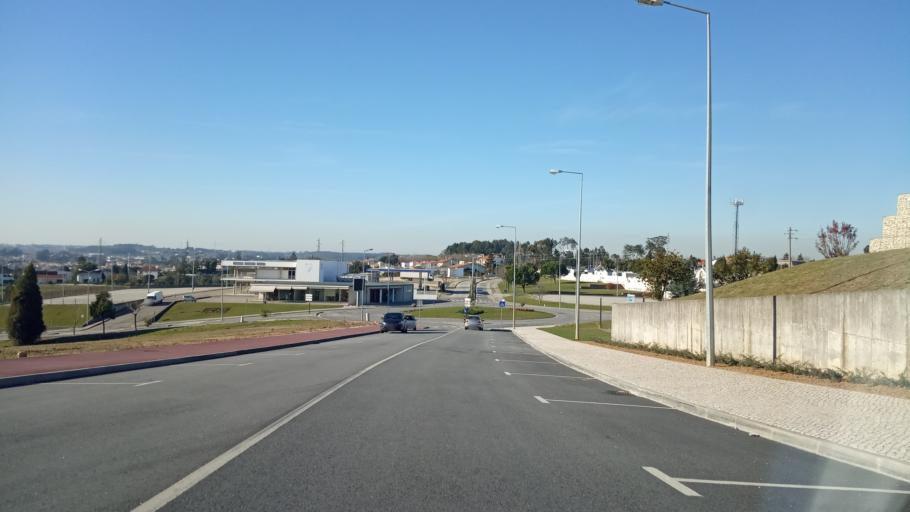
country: PT
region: Aveiro
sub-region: Anadia
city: Anadia
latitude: 40.4348
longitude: -8.4403
